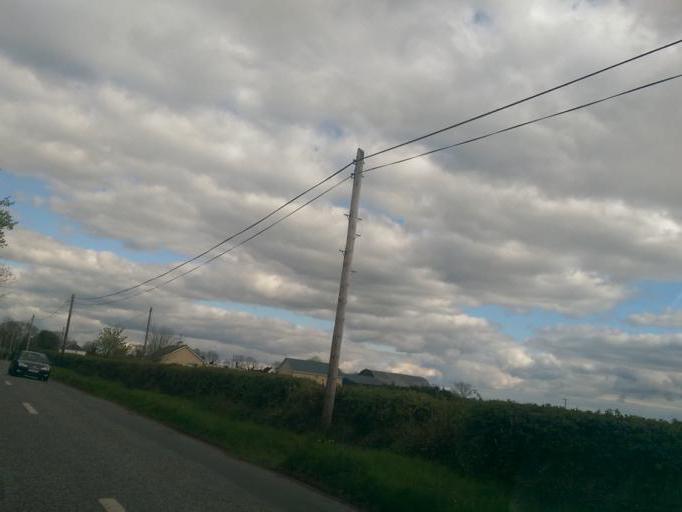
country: IE
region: Connaught
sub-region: County Galway
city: Ballinasloe
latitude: 53.4140
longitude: -8.3534
